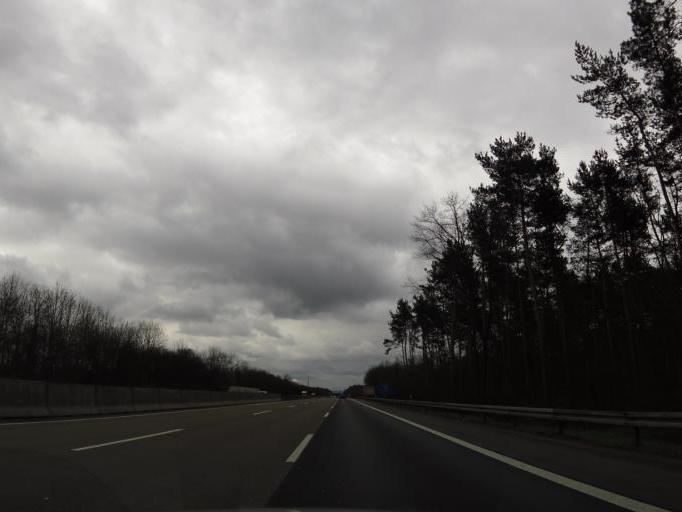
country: DE
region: Hesse
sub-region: Regierungsbezirk Darmstadt
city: Seligenstadt
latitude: 50.0102
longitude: 8.9751
